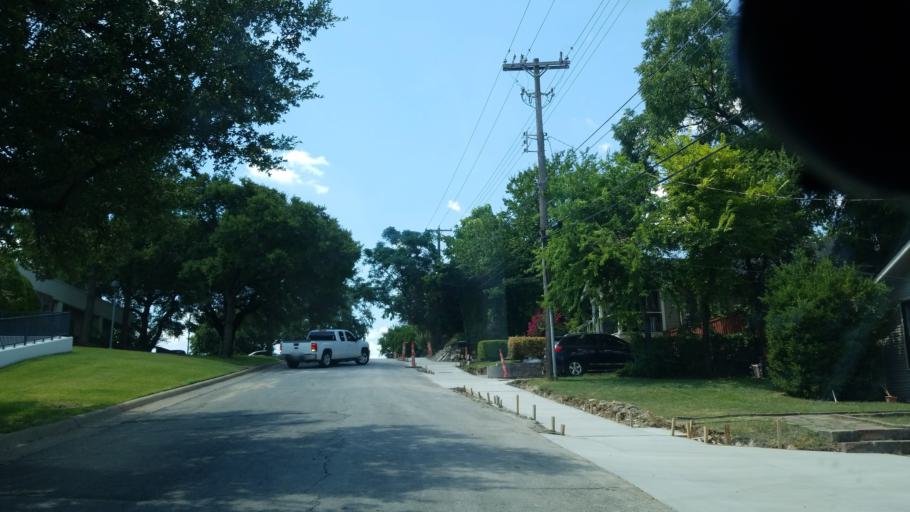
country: US
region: Texas
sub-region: Dallas County
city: Cockrell Hill
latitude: 32.7319
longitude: -96.8379
